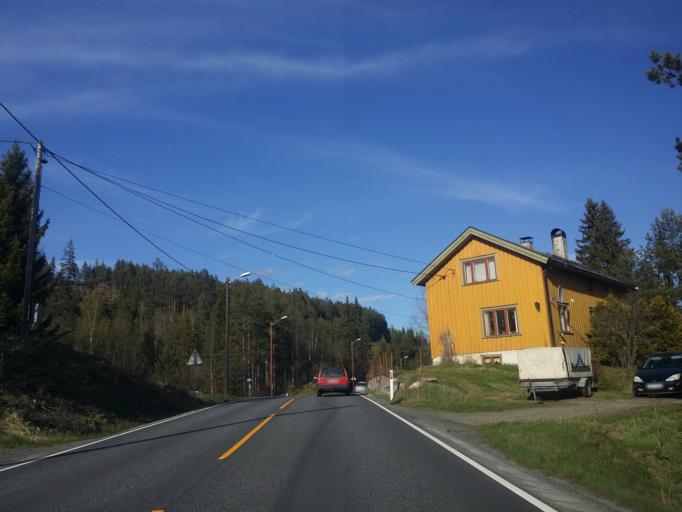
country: NO
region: Buskerud
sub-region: Kongsberg
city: Kongsberg
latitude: 59.6274
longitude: 9.4776
